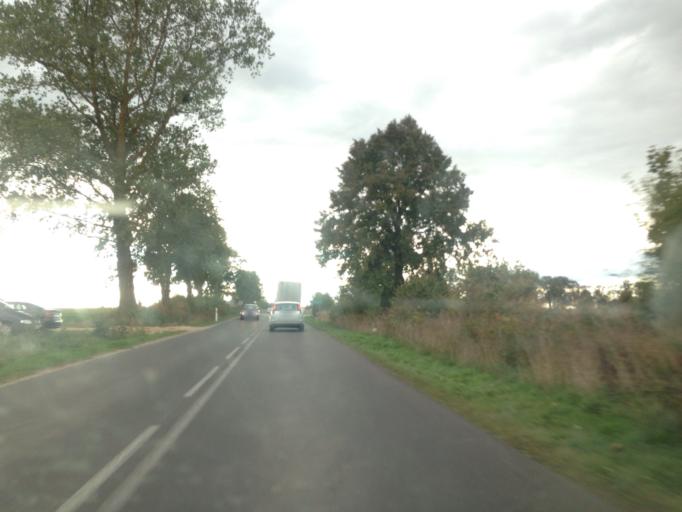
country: PL
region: Pomeranian Voivodeship
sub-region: Powiat kwidzynski
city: Kwidzyn
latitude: 53.7245
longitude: 19.0004
